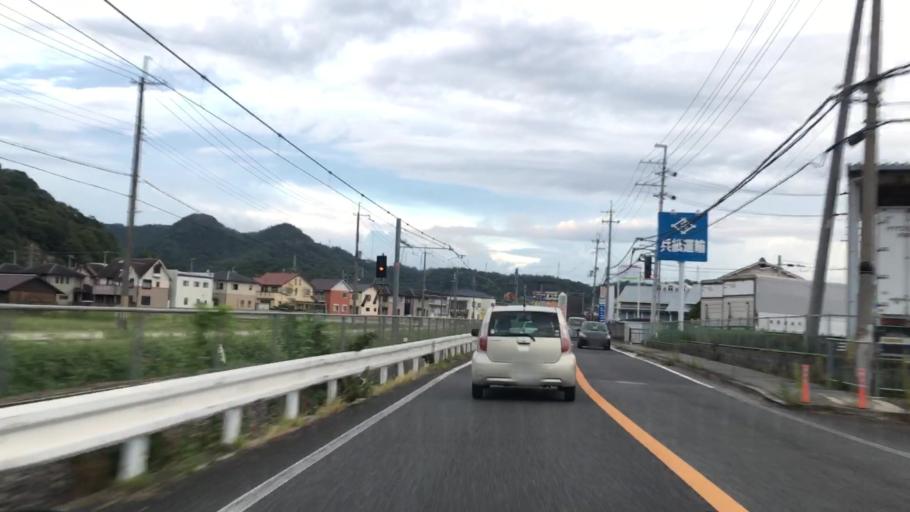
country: JP
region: Hyogo
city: Himeji
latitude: 34.8788
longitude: 134.7289
